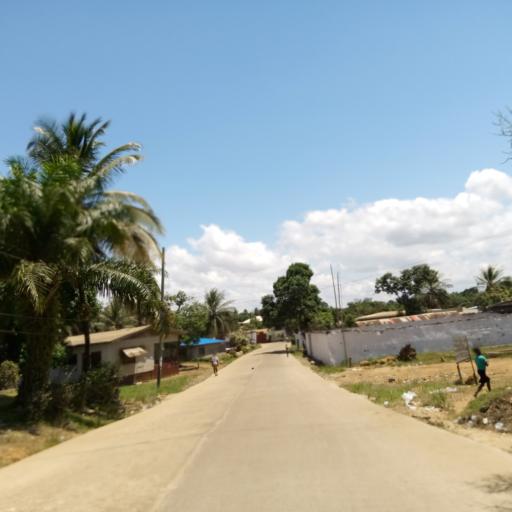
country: LR
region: Montserrado
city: Monrovia
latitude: 6.2449
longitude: -10.6920
